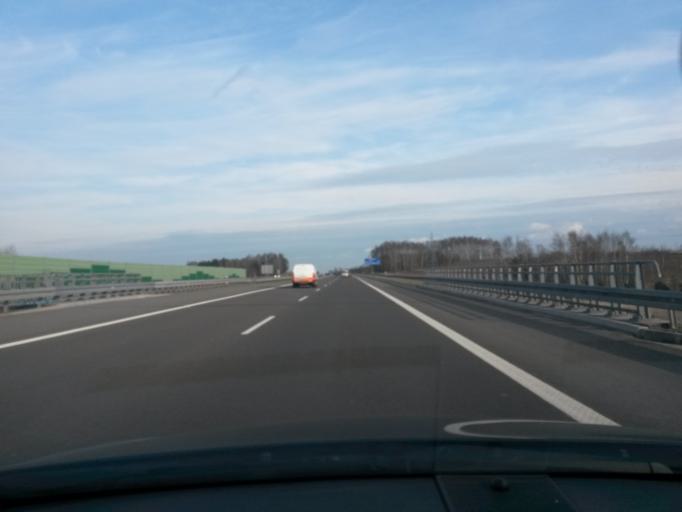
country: PL
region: Lodz Voivodeship
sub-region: Powiat zgierski
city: Zgierz
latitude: 51.9063
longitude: 19.4476
